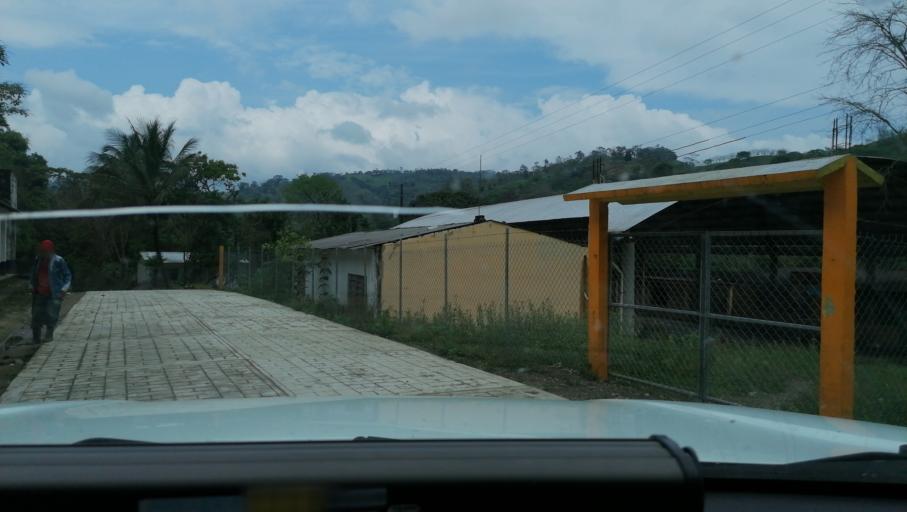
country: MX
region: Chiapas
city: Ocotepec
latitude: 17.3152
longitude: -93.1357
